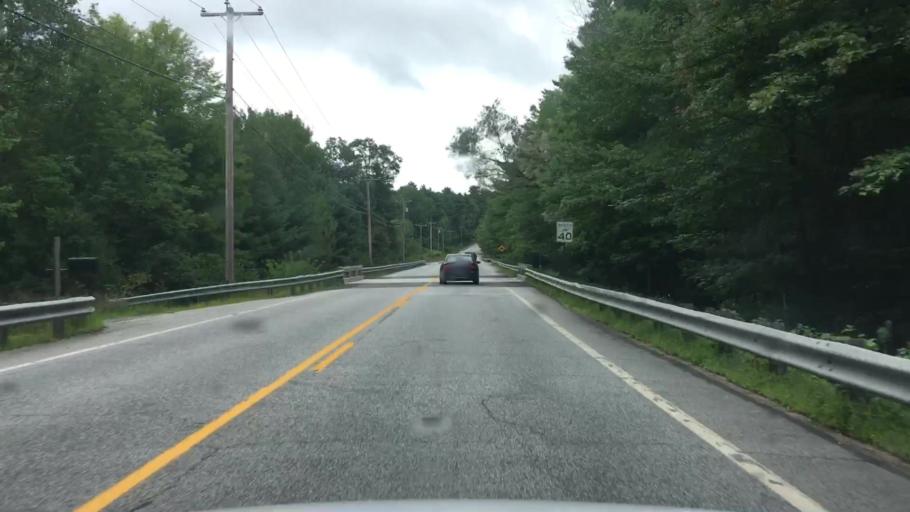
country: US
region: Maine
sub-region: Oxford County
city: Hiram
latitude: 43.8442
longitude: -70.7840
